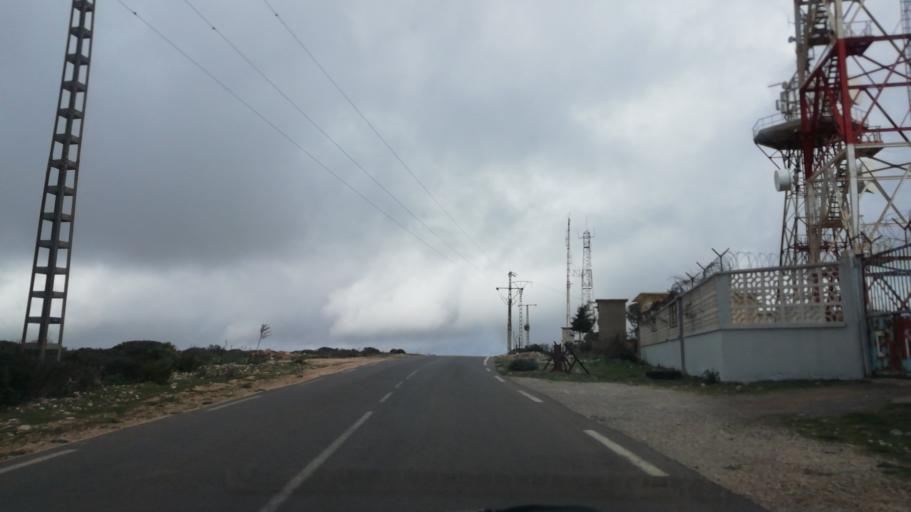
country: DZ
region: Oran
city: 'Ain el Turk
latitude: 35.6961
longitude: -0.7716
